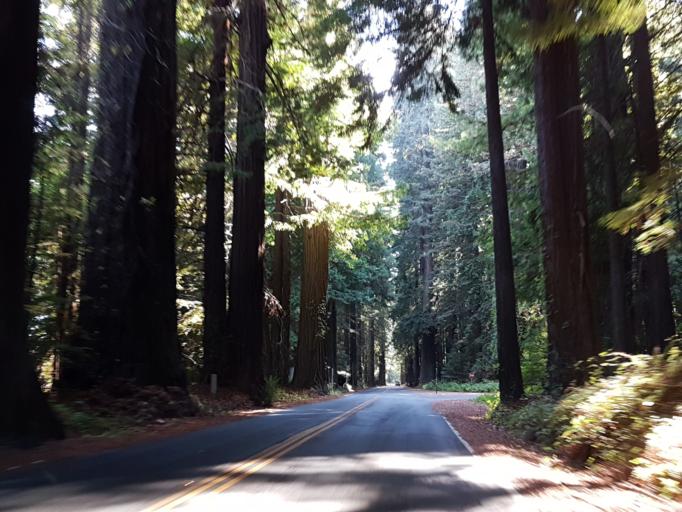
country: US
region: California
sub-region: Humboldt County
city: Rio Dell
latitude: 40.4370
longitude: -123.9852
